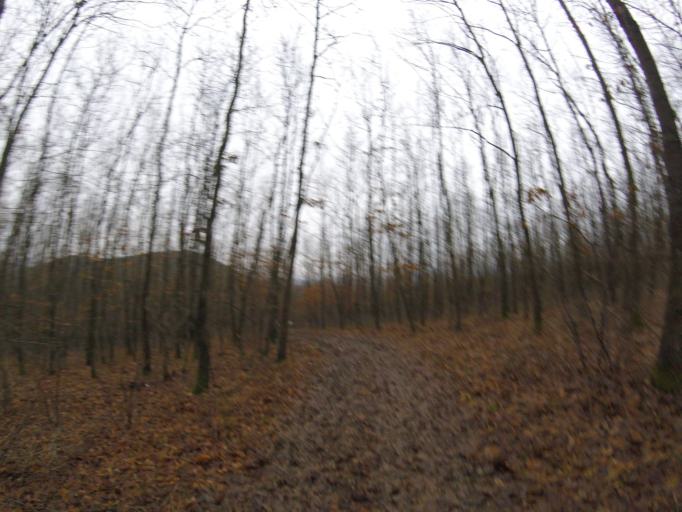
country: HU
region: Pest
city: Veroce
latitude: 47.8424
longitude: 19.0308
